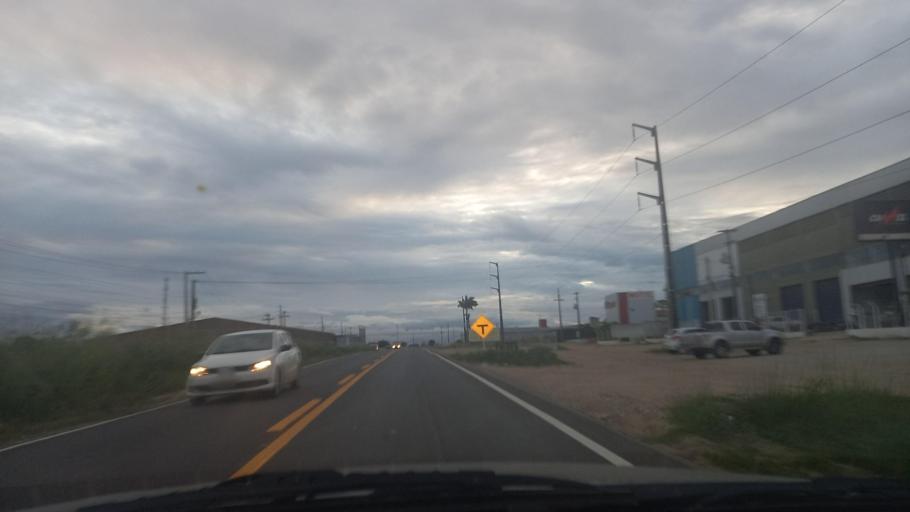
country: BR
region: Pernambuco
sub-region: Caruaru
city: Caruaru
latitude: -8.2532
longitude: -35.9720
